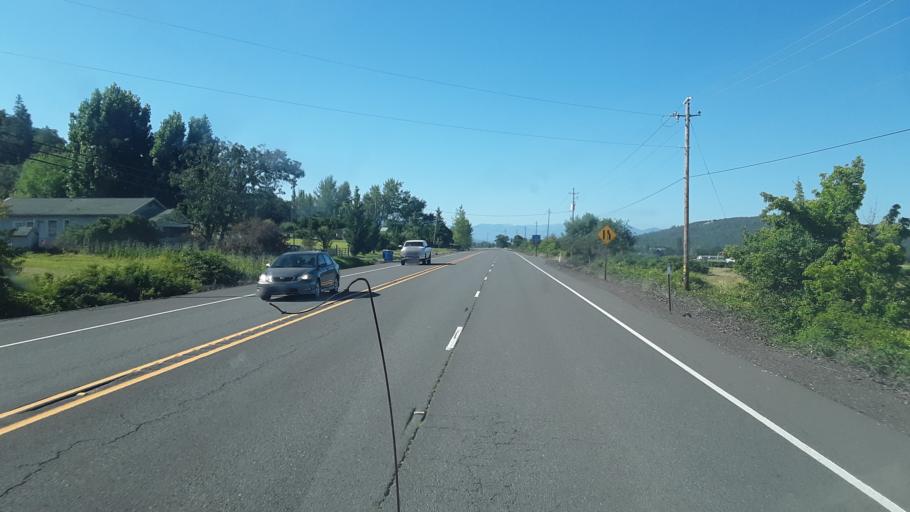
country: US
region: Oregon
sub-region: Jackson County
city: Eagle Point
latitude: 42.5294
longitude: -122.8145
